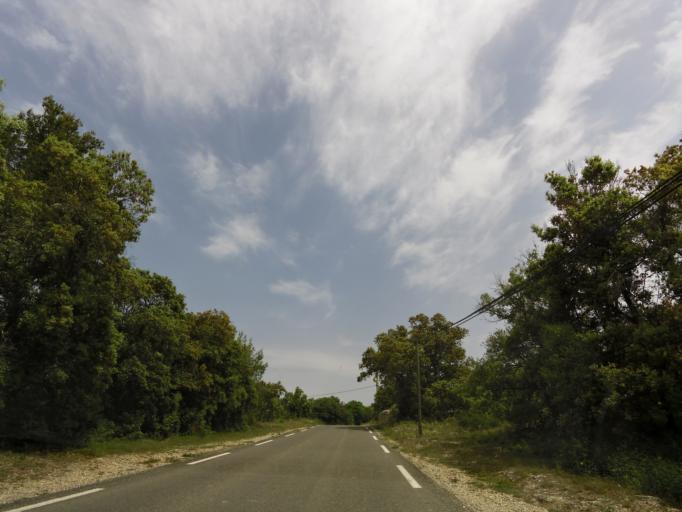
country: FR
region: Languedoc-Roussillon
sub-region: Departement du Gard
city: Aubais
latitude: 43.7630
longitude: 4.1192
